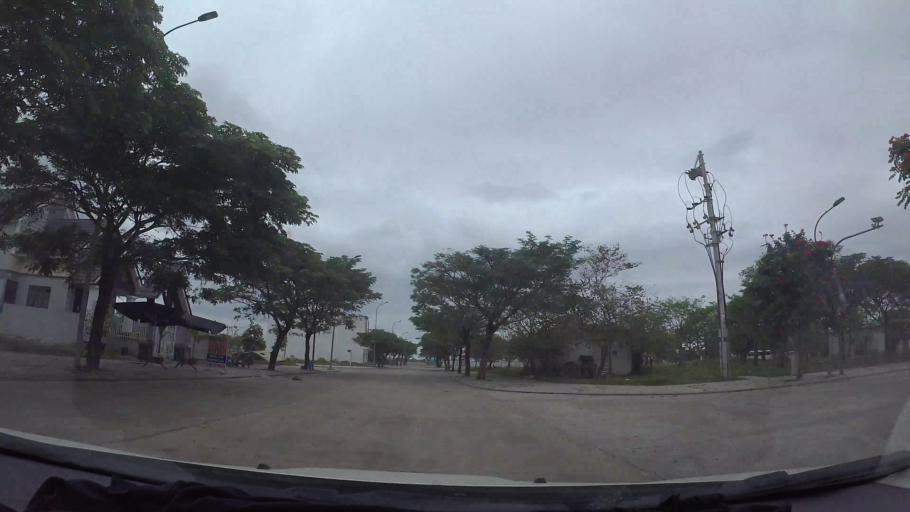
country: VN
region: Da Nang
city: Lien Chieu
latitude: 16.1053
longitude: 108.1194
